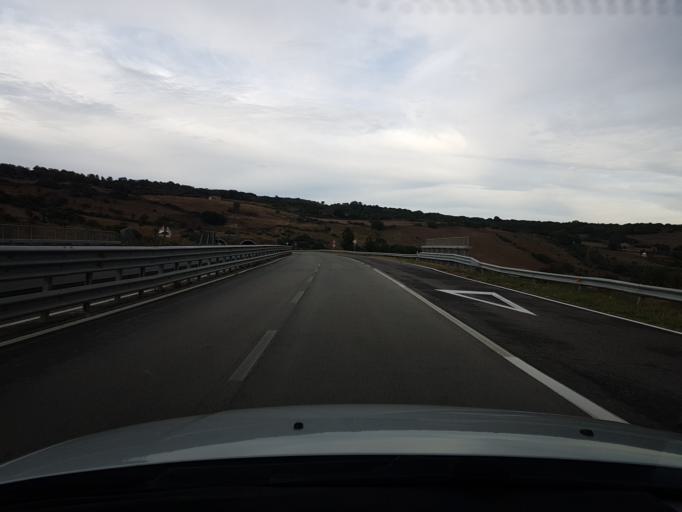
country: IT
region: Sardinia
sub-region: Provincia di Oristano
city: Sedilo
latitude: 40.1651
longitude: 8.9274
